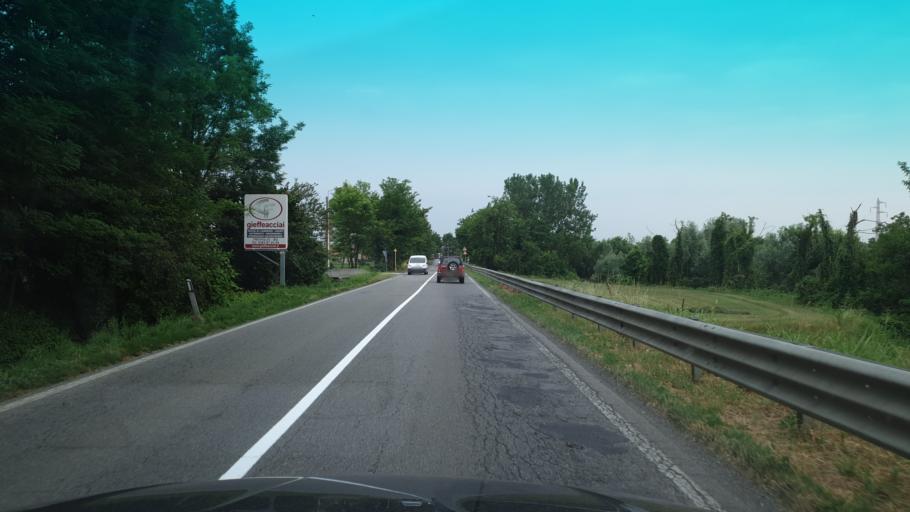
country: IT
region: Lombardy
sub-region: Provincia di Bergamo
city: Badalasco
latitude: 45.5315
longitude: 9.5380
